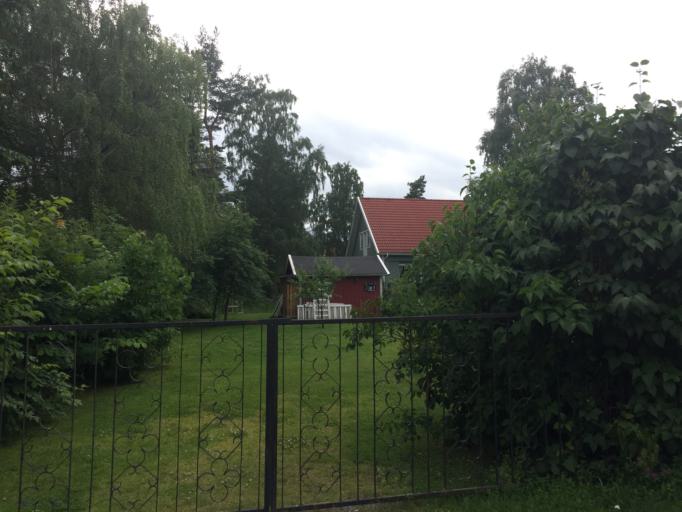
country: SE
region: Stockholm
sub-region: Botkyrka Kommun
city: Tullinge
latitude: 59.1941
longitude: 17.8964
